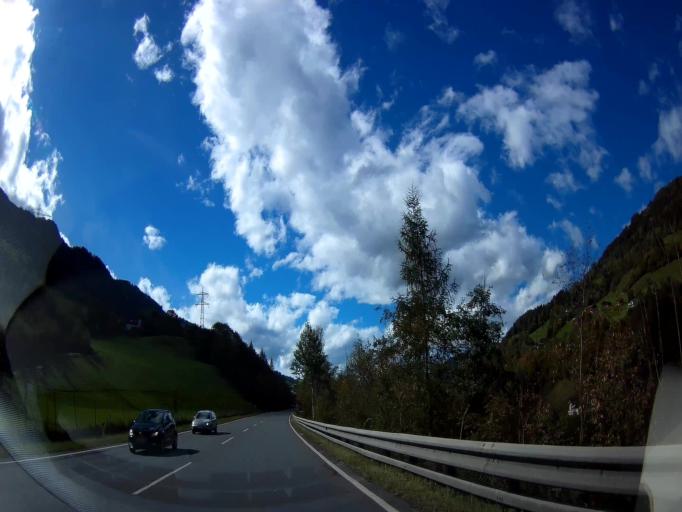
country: AT
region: Salzburg
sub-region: Politischer Bezirk Zell am See
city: Lend
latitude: 47.2973
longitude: 13.0738
